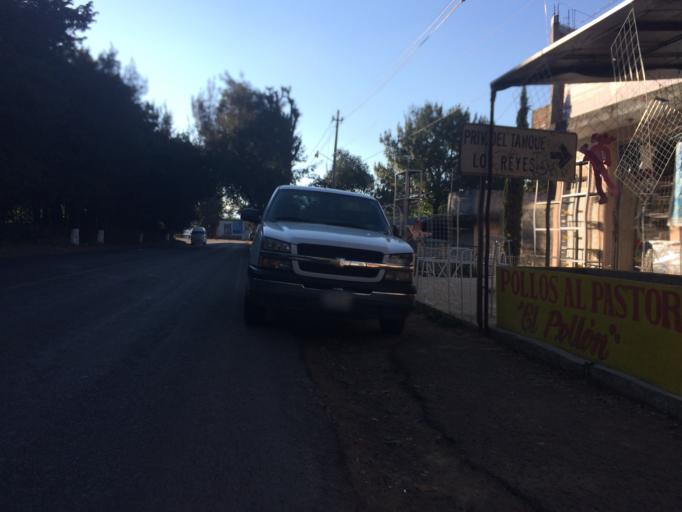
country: MX
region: Michoacan
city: Patzcuaro
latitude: 19.5064
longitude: -101.6080
